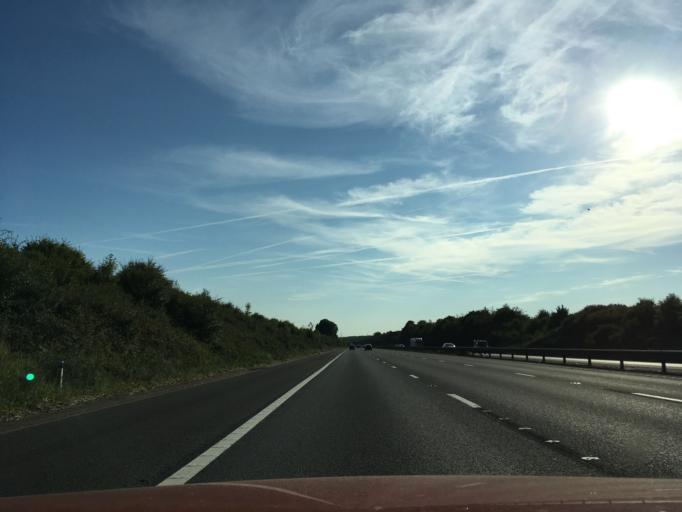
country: GB
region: England
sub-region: South Gloucestershire
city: Alveston
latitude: 51.5793
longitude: -2.5109
